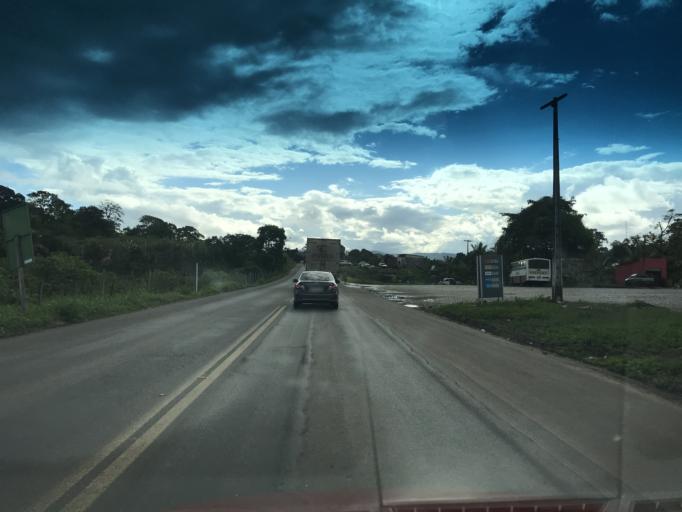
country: BR
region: Bahia
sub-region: Ibirapitanga
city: Ibirapitanga
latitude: -14.1510
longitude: -39.3322
